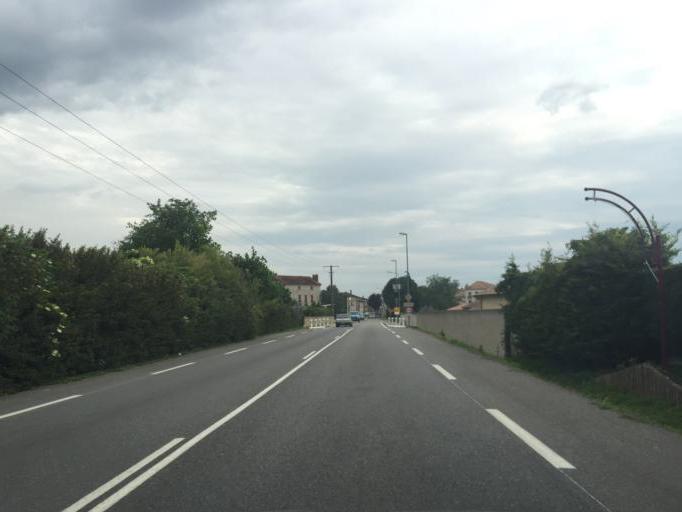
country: FR
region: Rhone-Alpes
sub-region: Departement de la Drome
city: Alixan
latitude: 44.9776
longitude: 5.0284
